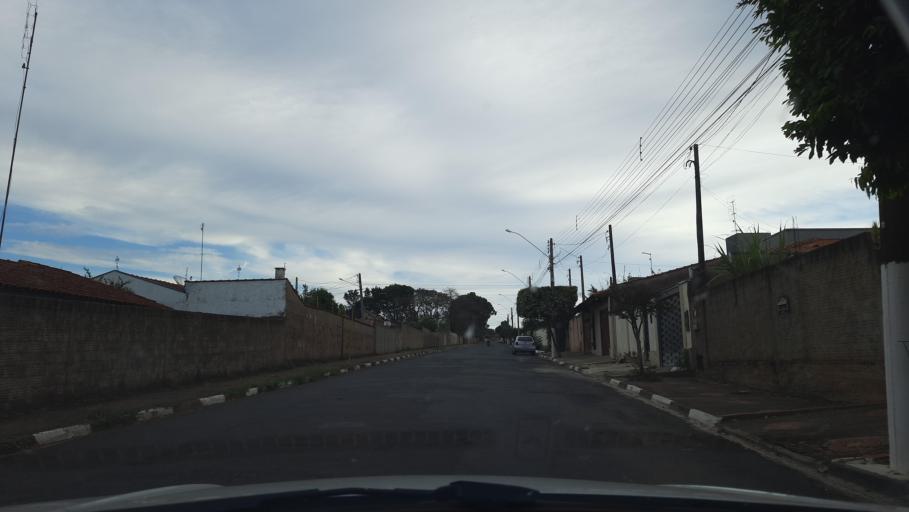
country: BR
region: Sao Paulo
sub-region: Casa Branca
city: Casa Branca
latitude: -21.7846
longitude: -47.0893
